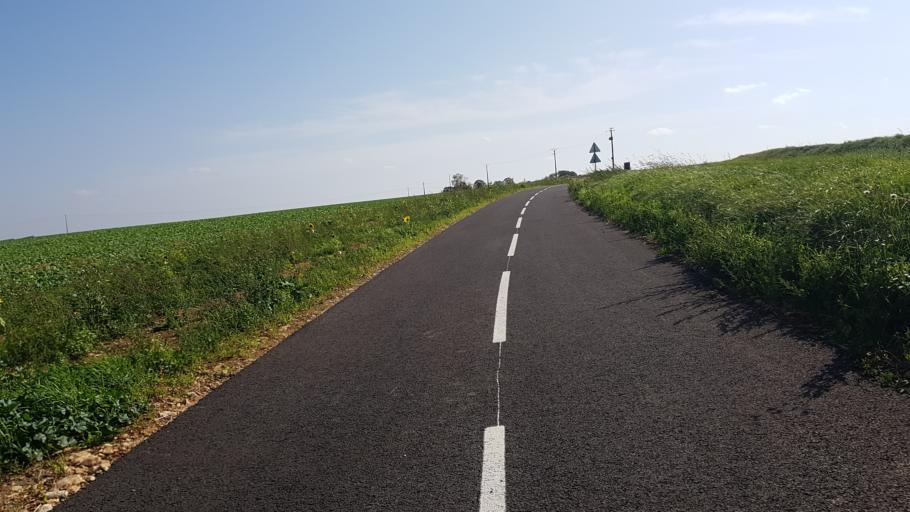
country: FR
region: Poitou-Charentes
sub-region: Departement de la Vienne
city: Chasseneuil-du-Poitou
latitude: 46.6597
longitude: 0.3440
